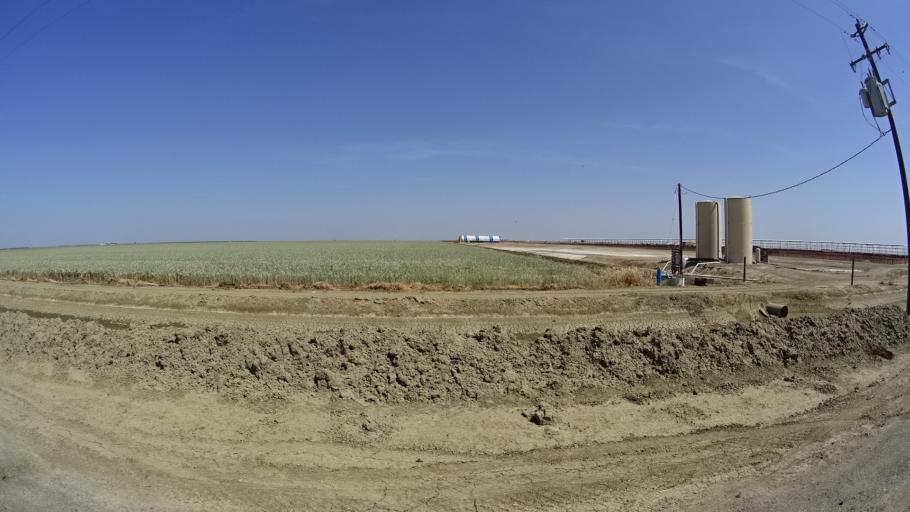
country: US
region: California
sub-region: Kings County
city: Kettleman City
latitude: 36.0941
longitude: -119.9373
